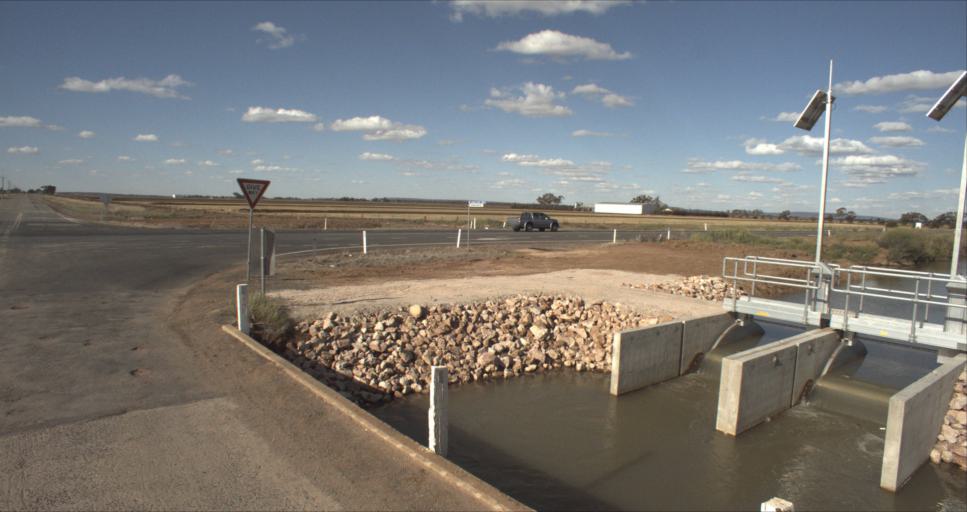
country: AU
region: New South Wales
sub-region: Leeton
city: Leeton
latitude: -34.5202
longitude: 146.2834
